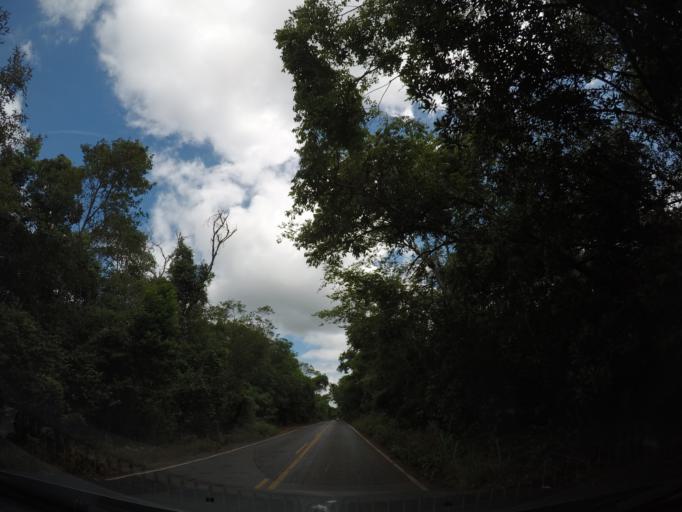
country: BR
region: Bahia
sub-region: Andarai
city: Vera Cruz
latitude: -12.5115
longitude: -41.3618
